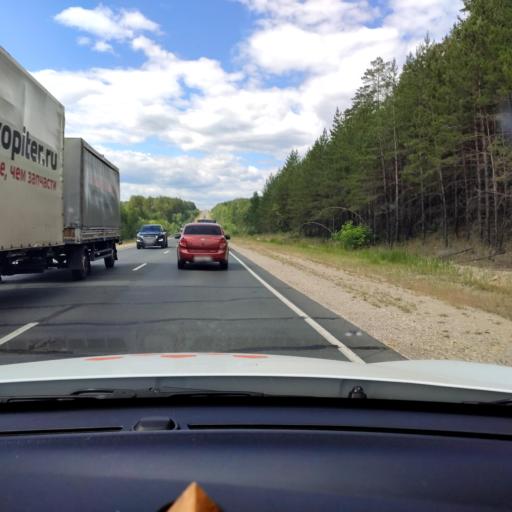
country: RU
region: Mariy-El
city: Volzhsk
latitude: 55.8979
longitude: 48.3903
